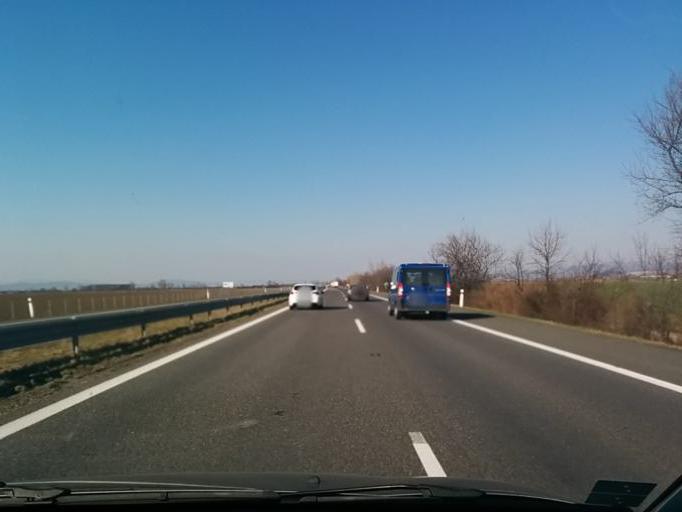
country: SK
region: Trnavsky
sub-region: Okres Trnava
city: Piestany
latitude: 48.5352
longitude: 17.7836
